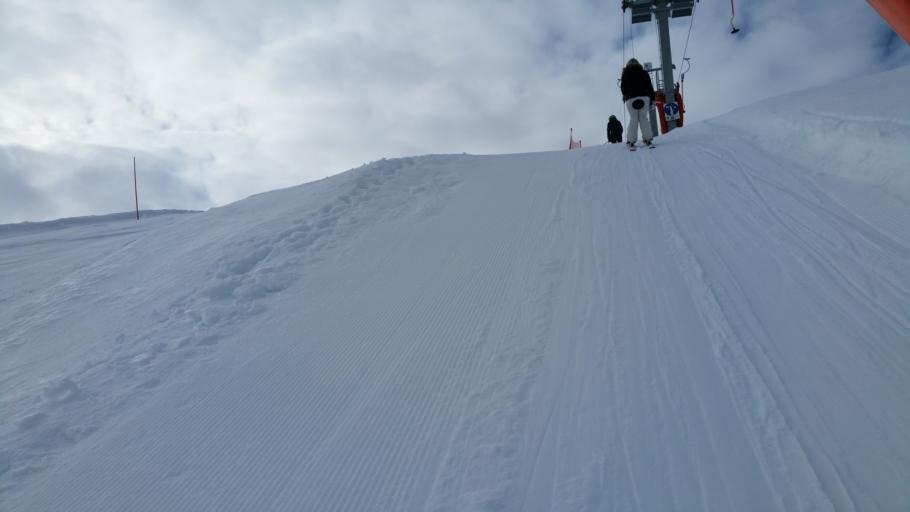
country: FR
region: Rhone-Alpes
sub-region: Departement de la Savoie
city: Saint-Jean-de-Maurienne
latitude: 45.2652
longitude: 6.2701
